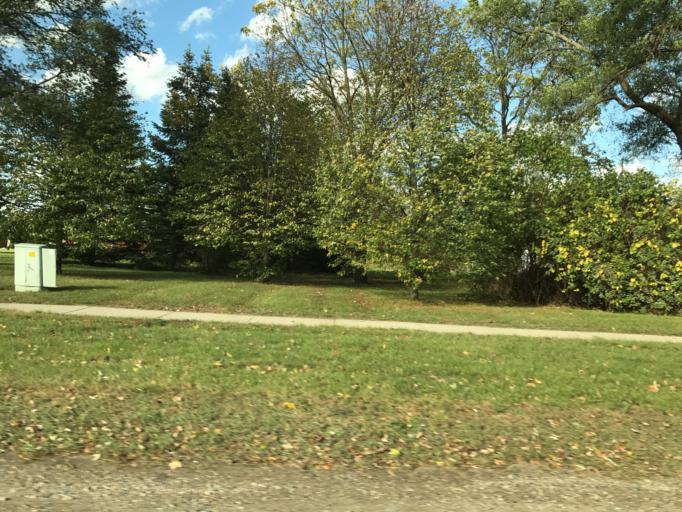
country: US
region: Michigan
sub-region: Oakland County
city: South Lyon
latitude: 42.5108
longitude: -83.6118
